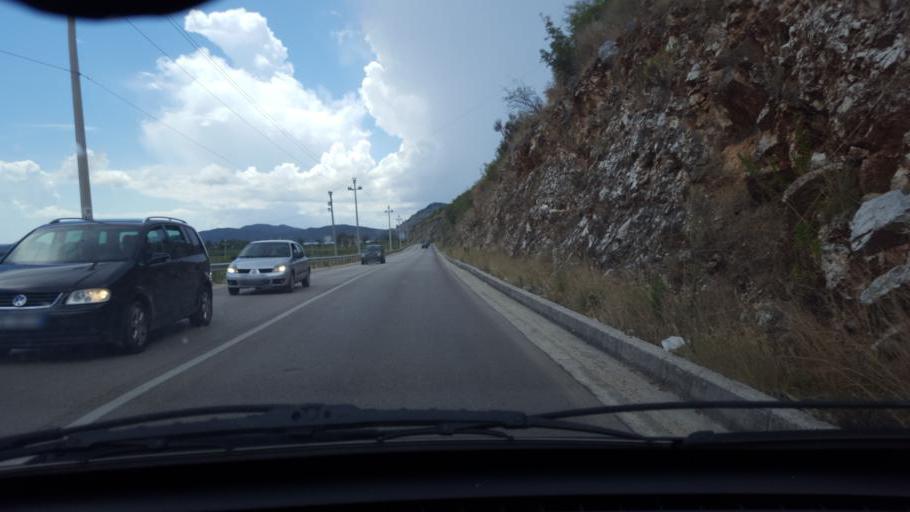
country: AL
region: Vlore
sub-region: Rrethi i Sarandes
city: Sarande
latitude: 39.8267
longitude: 20.0221
